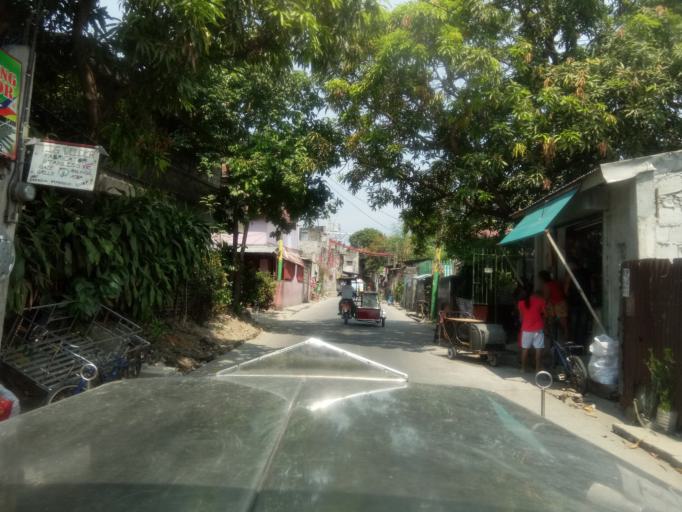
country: PH
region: Calabarzon
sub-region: Province of Cavite
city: Dasmarinas
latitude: 14.3200
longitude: 120.9796
